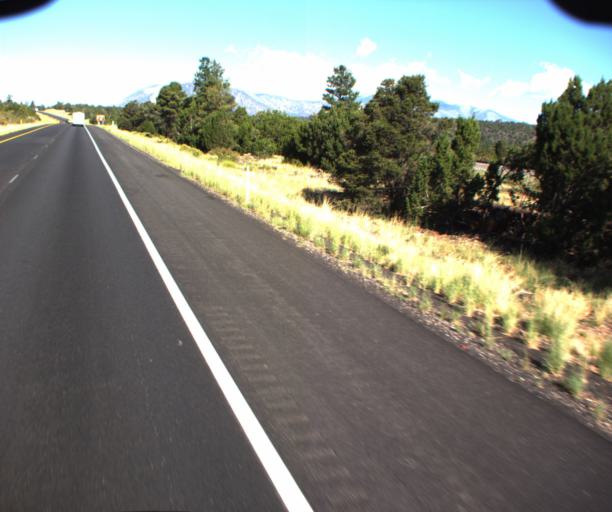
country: US
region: Arizona
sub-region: Coconino County
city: Flagstaff
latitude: 35.2056
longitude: -111.4962
